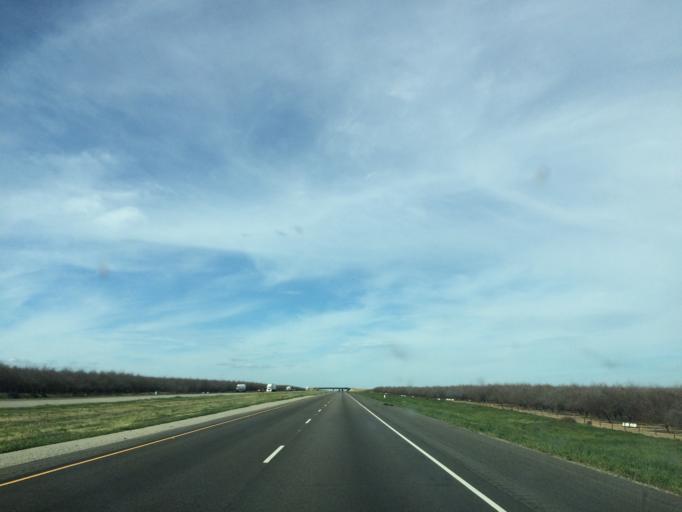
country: US
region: California
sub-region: Merced County
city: South Dos Palos
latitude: 36.7504
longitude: -120.7048
